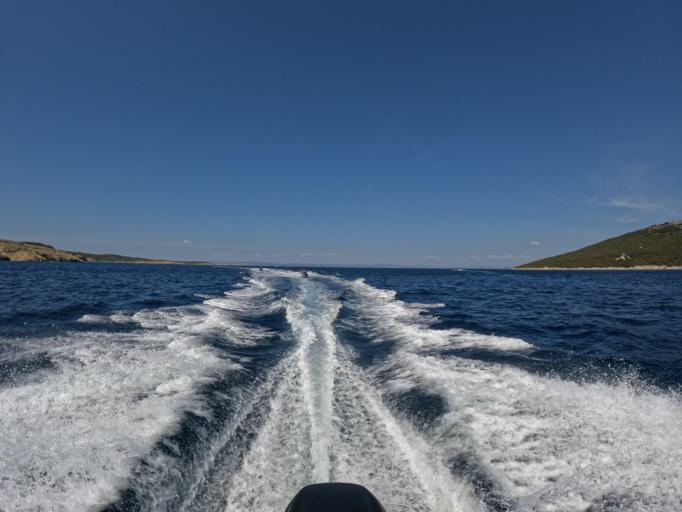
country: HR
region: Primorsko-Goranska
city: Lopar
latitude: 44.8522
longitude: 14.7536
